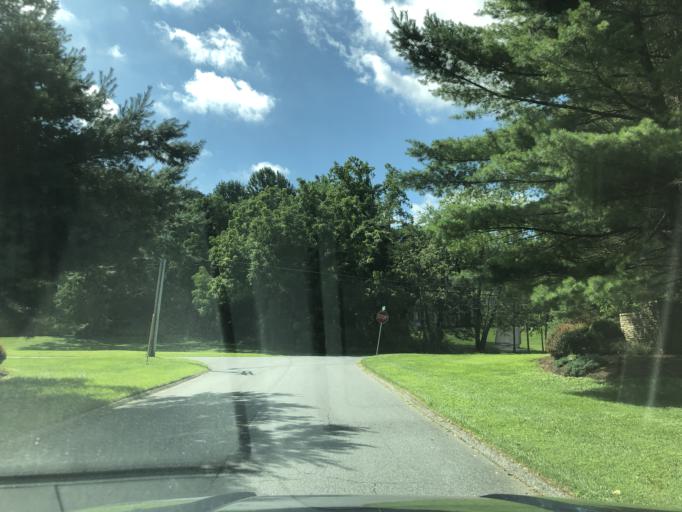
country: US
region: Maryland
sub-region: Howard County
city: Highland
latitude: 39.2022
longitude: -76.9891
